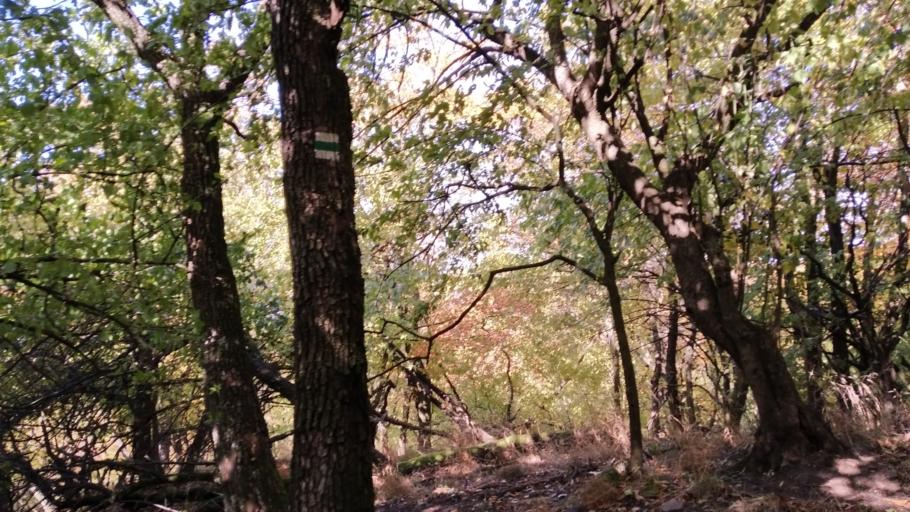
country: HU
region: Pest
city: Visegrad
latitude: 47.7456
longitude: 18.9656
